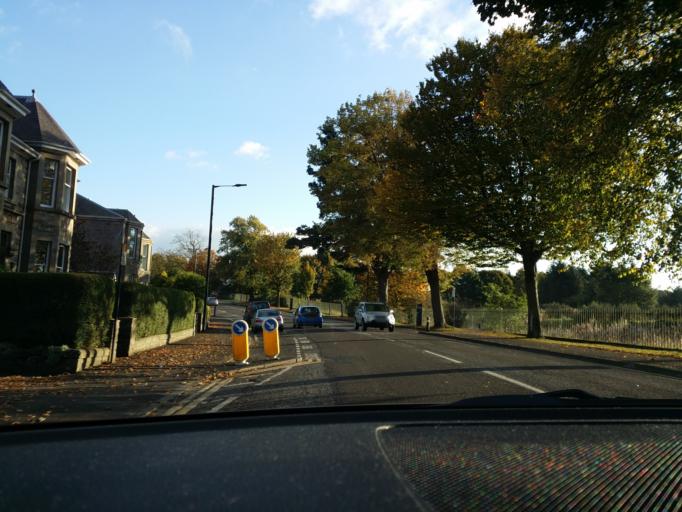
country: GB
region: Scotland
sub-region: Stirling
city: Stirling
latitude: 56.1174
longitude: -3.9482
